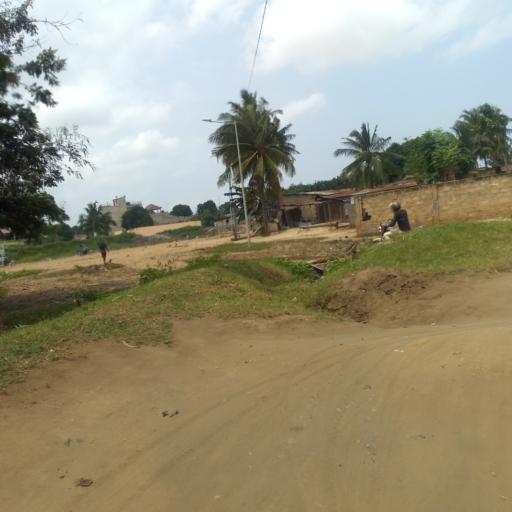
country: TG
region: Maritime
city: Lome
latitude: 6.1880
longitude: 1.1739
